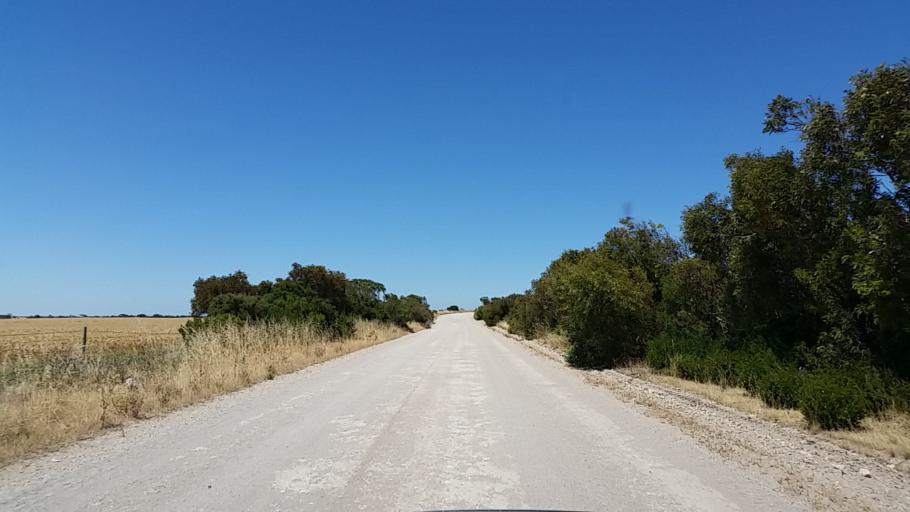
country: AU
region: South Australia
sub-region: Yorke Peninsula
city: Honiton
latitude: -35.0917
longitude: 137.4501
